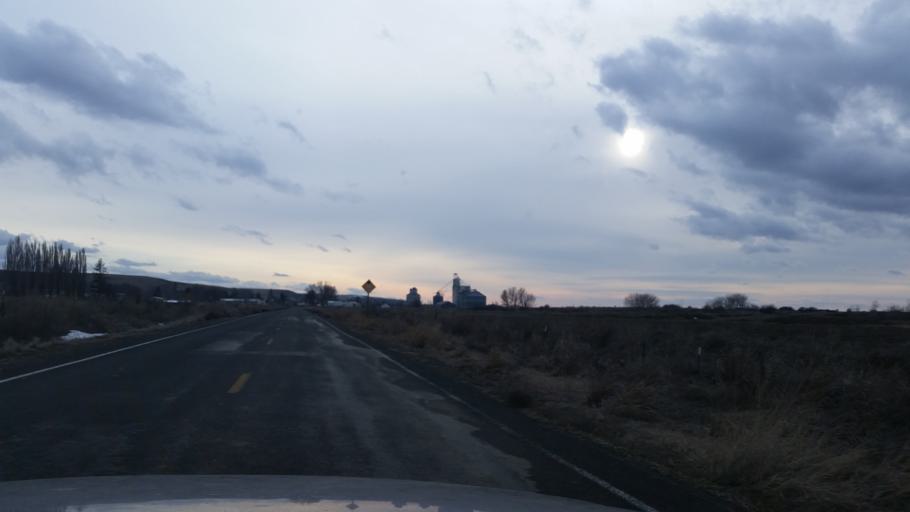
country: US
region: Washington
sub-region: Spokane County
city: Medical Lake
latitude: 47.2077
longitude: -117.8989
